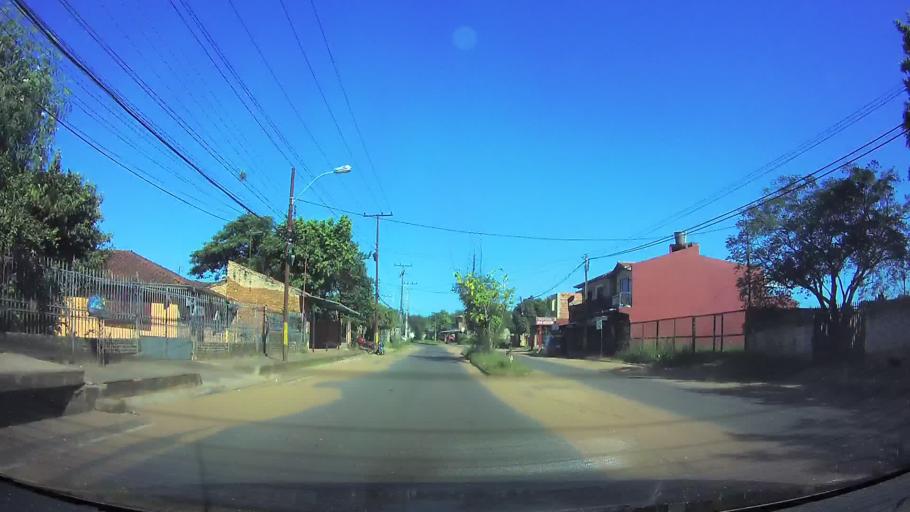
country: PY
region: Central
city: Fernando de la Mora
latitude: -25.2975
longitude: -57.5123
